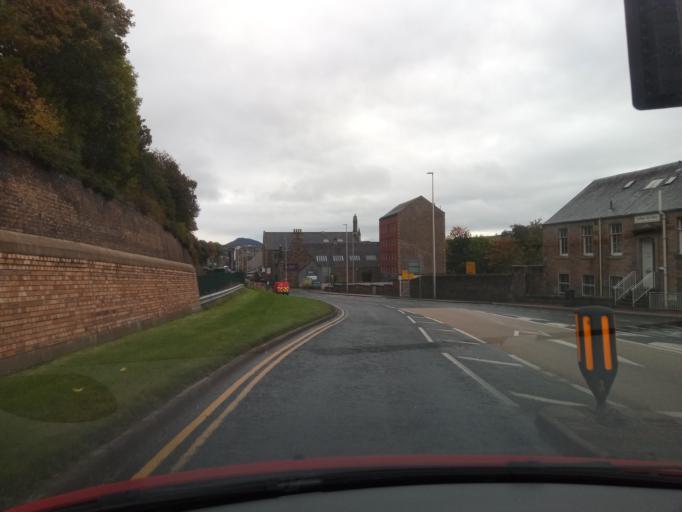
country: GB
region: Scotland
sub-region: The Scottish Borders
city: Galashiels
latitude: 55.6194
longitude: -2.8102
